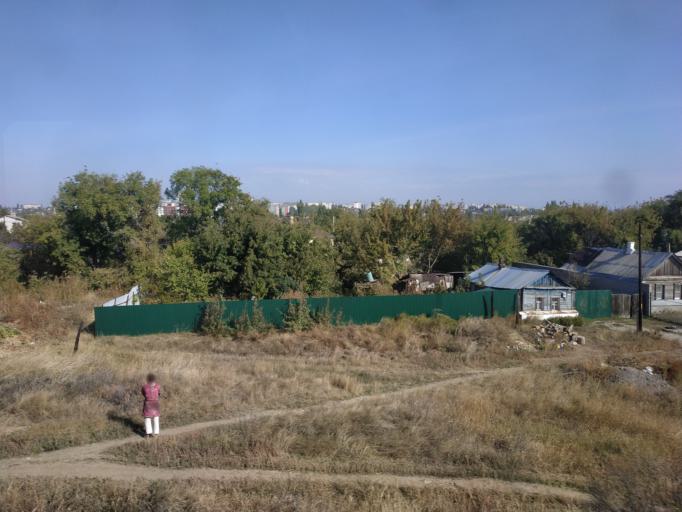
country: RU
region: Volgograd
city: Volgograd
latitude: 48.7491
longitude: 44.5370
